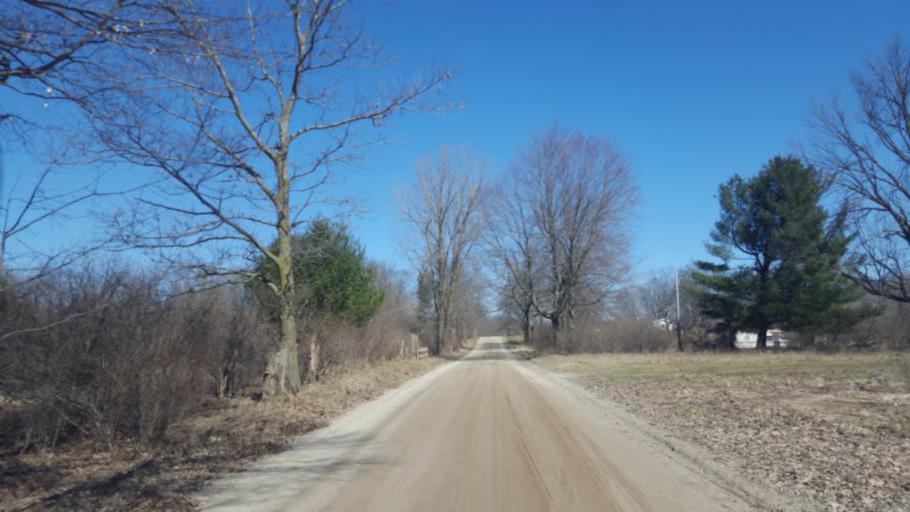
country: US
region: Michigan
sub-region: Montcalm County
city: Edmore
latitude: 43.4564
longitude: -85.0850
